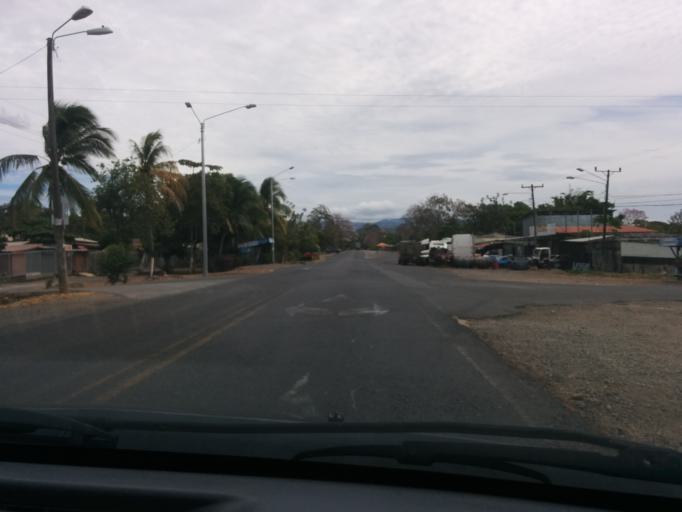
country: CR
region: Puntarenas
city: Esparza
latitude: 10.0003
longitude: -84.6469
